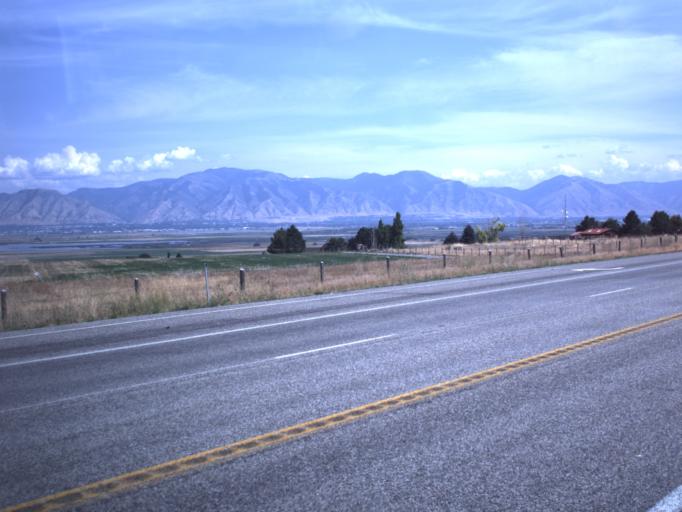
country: US
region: Utah
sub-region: Cache County
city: Mendon
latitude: 41.7634
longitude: -112.0093
